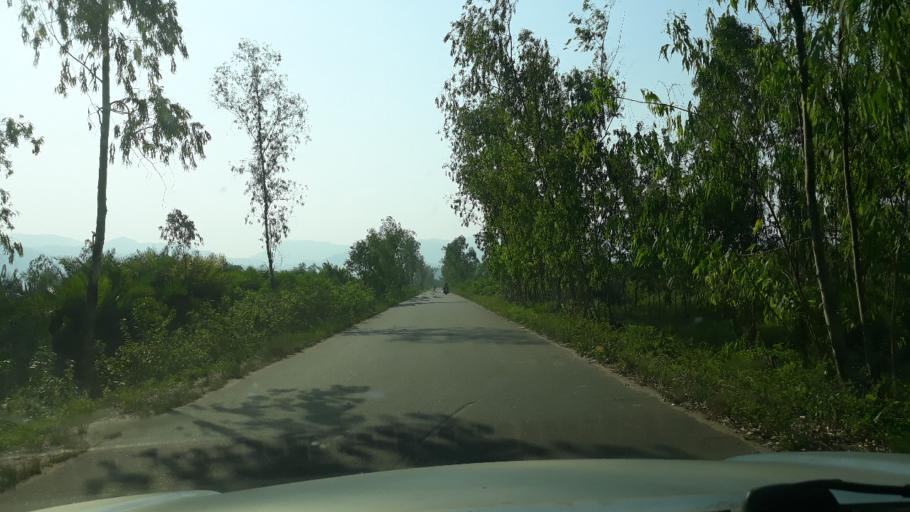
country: BI
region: Cibitoke
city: Cibitoke
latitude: -2.8145
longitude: 29.0043
